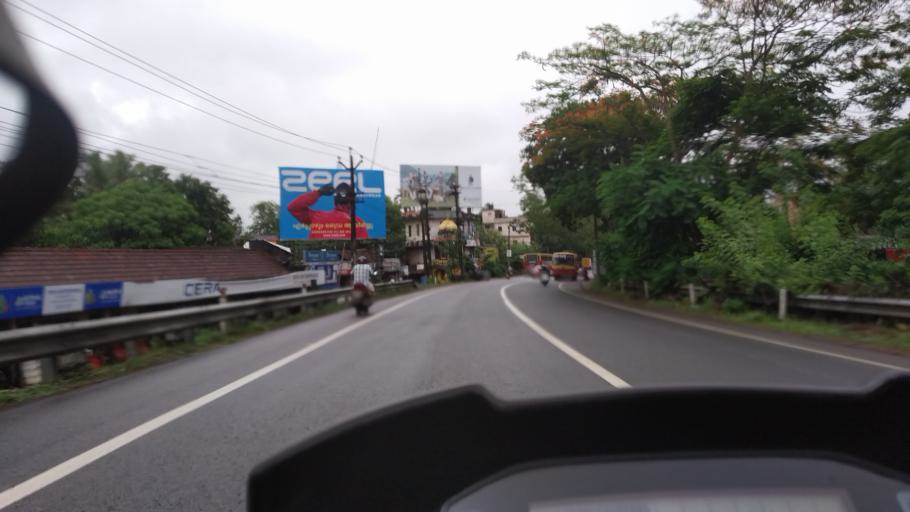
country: IN
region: Kerala
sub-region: Alappuzha
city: Mavelikara
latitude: 9.2830
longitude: 76.4420
